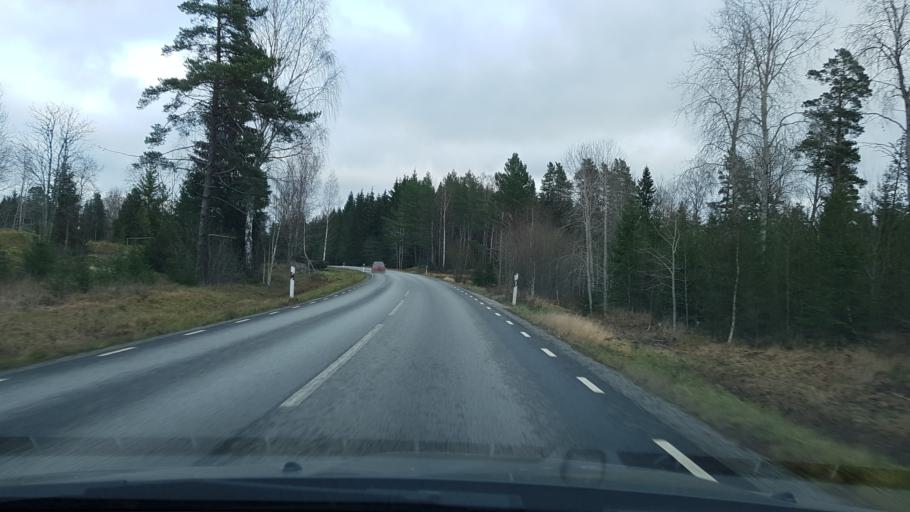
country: SE
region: Stockholm
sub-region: Norrtalje Kommun
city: Hallstavik
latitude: 60.0365
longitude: 18.5079
